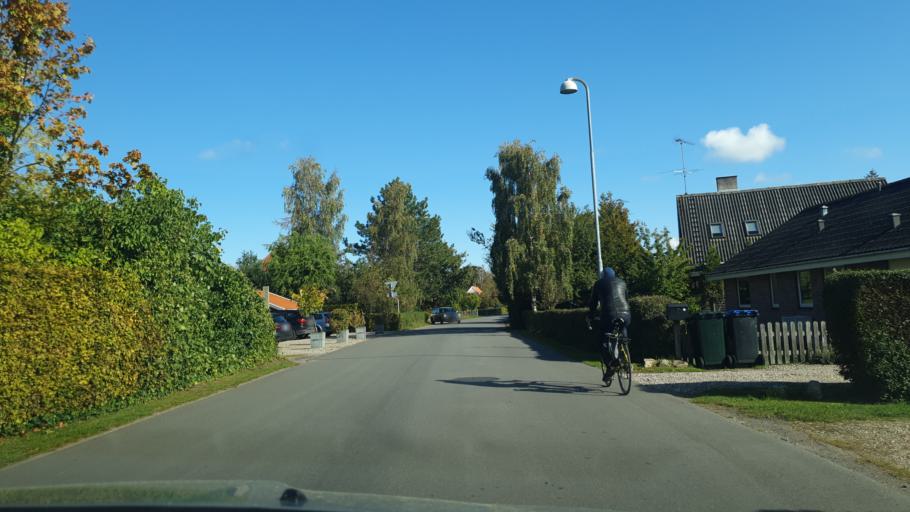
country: DK
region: Zealand
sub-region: Odsherred Kommune
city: Nykobing Sjaelland
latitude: 55.9442
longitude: 11.7554
